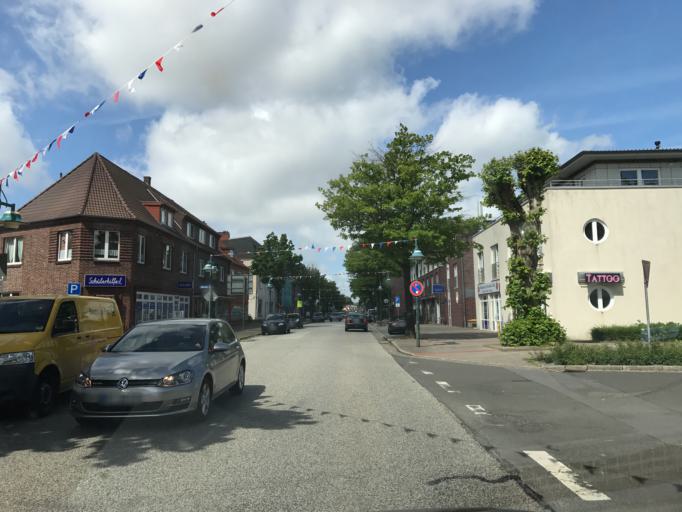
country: DE
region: Schleswig-Holstein
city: Brunsbuttel
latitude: 53.8971
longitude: 9.1353
